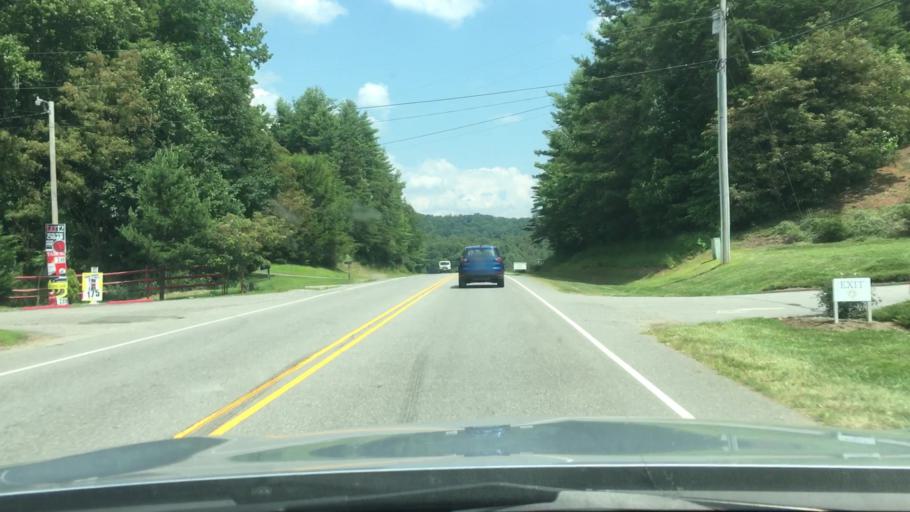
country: US
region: North Carolina
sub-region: Madison County
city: Mars Hill
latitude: 35.8258
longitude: -82.5696
